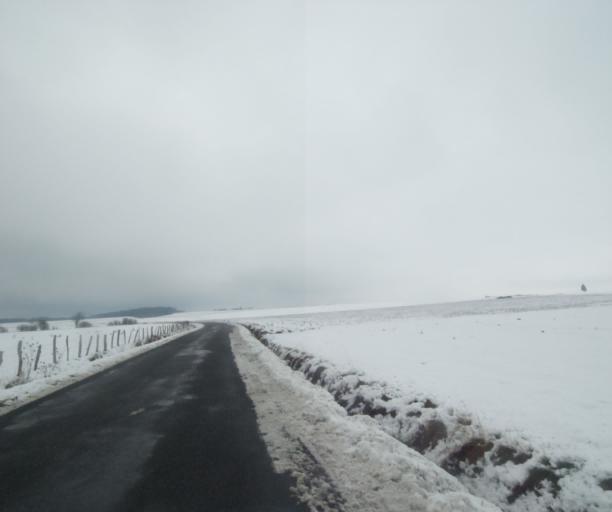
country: FR
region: Champagne-Ardenne
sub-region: Departement de la Haute-Marne
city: Montier-en-Der
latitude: 48.4712
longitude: 4.7936
